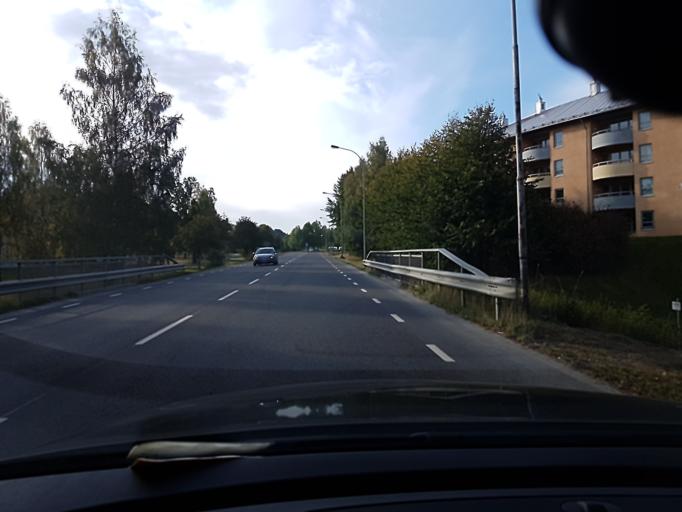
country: SE
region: Kronoberg
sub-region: Vaxjo Kommun
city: Vaexjoe
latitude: 56.8525
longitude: 14.8227
